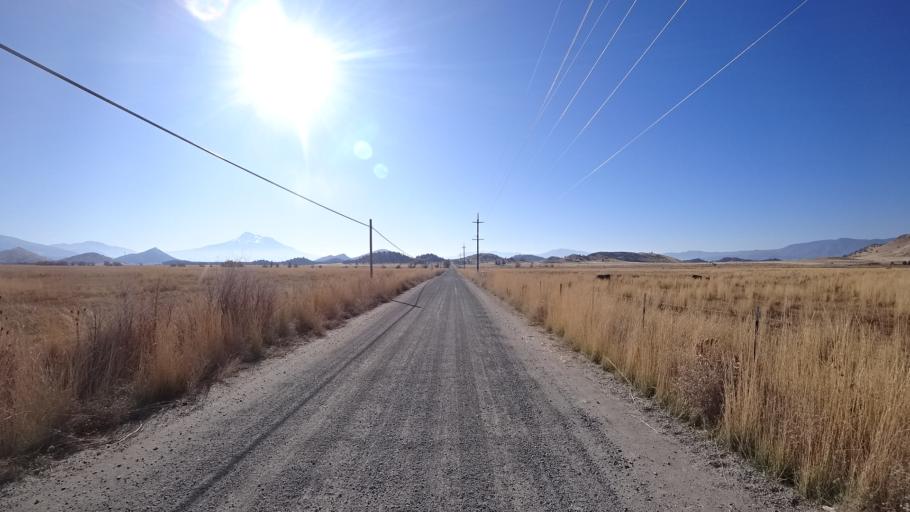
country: US
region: California
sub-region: Siskiyou County
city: Montague
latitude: 41.7112
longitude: -122.4377
